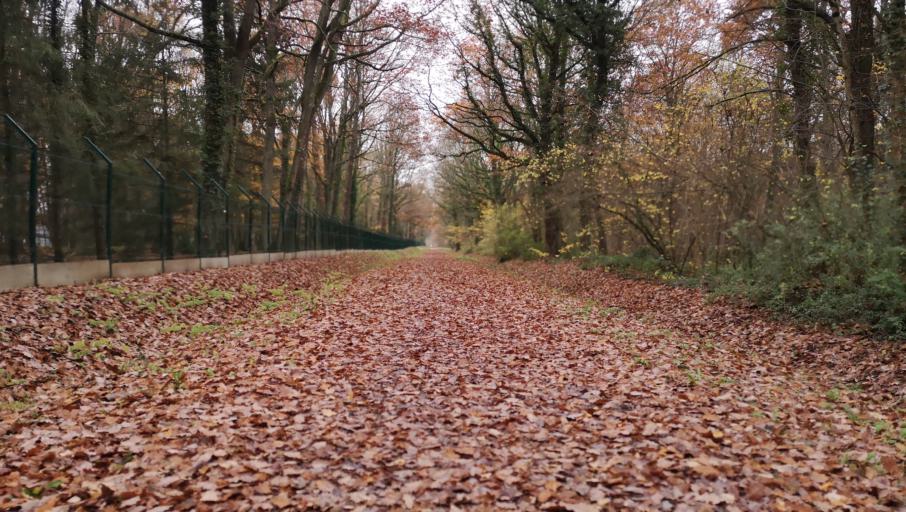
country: FR
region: Centre
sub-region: Departement du Loiret
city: Saint-Jean-de-Braye
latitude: 47.9311
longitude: 1.9892
